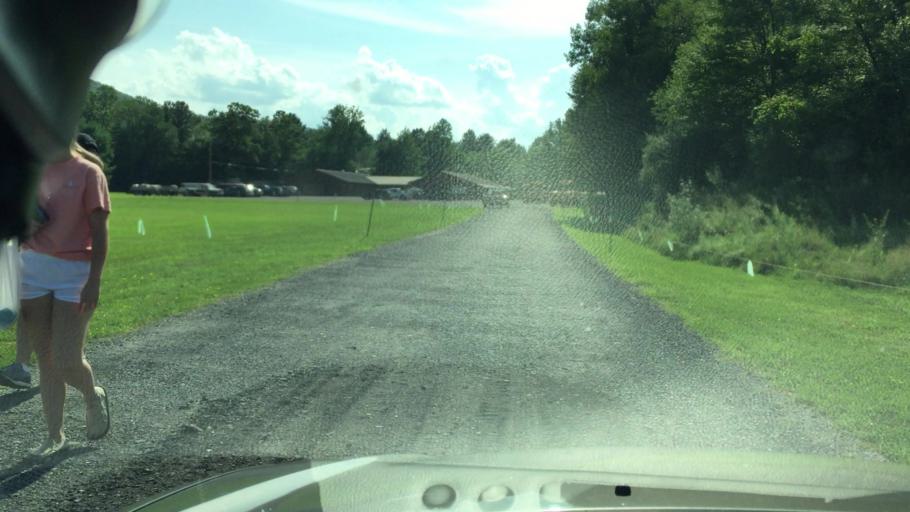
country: US
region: Pennsylvania
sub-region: Carbon County
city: Nesquehoning
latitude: 40.8703
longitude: -75.7947
